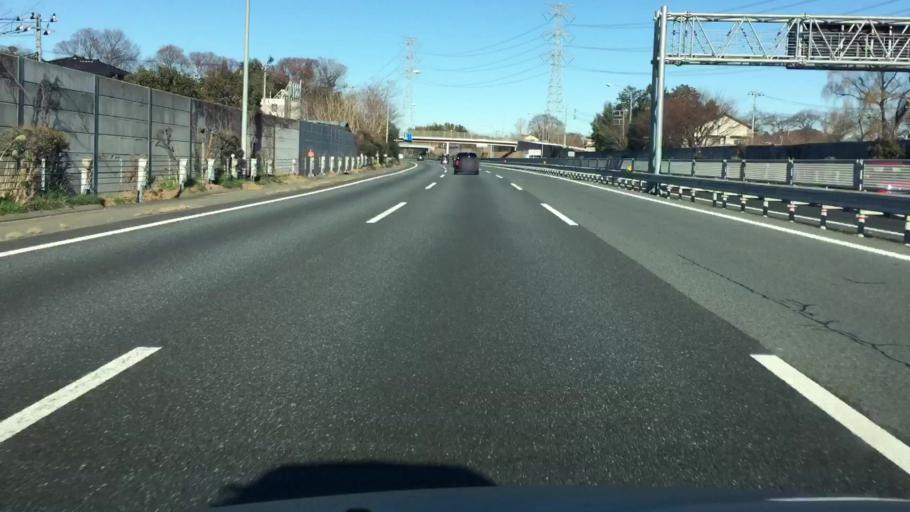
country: JP
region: Saitama
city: Sakado
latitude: 36.0319
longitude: 139.3799
